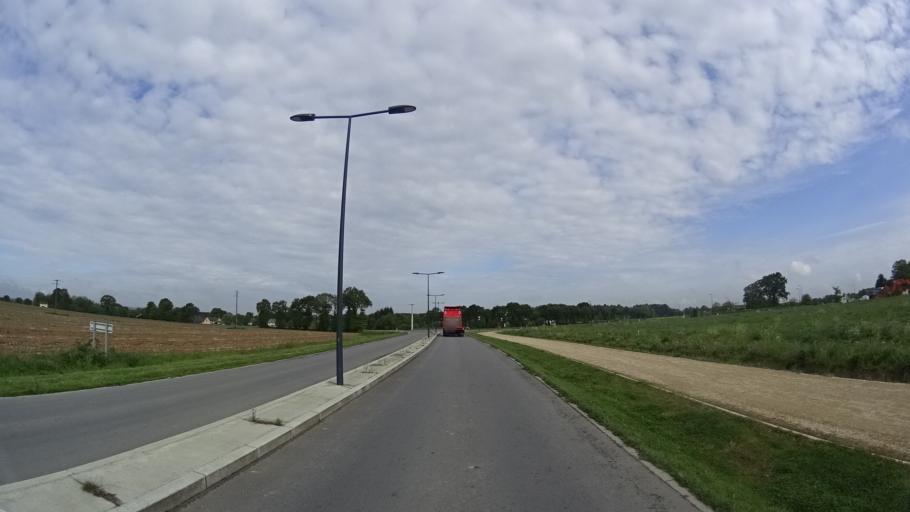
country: FR
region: Brittany
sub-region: Departement d'Ille-et-Vilaine
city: Mordelles
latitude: 48.0825
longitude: -1.8368
